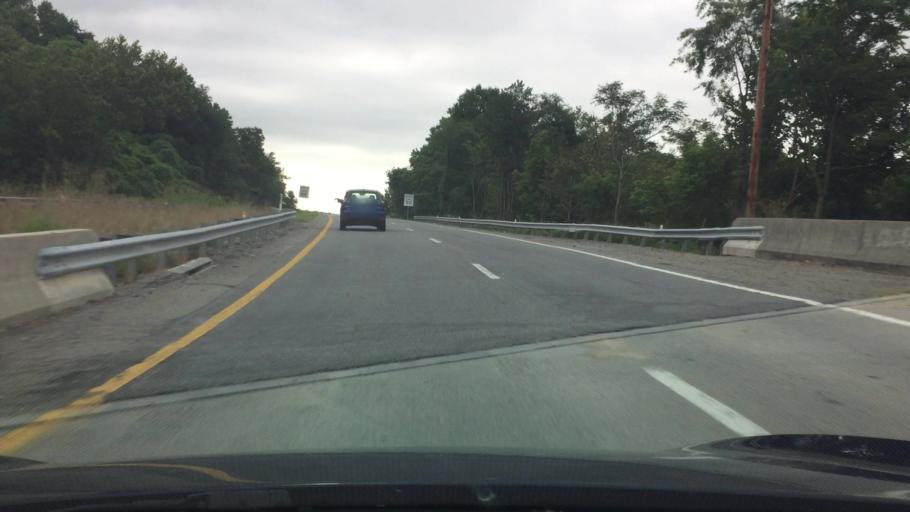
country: US
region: Virginia
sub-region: Montgomery County
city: Shawsville
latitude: 37.2221
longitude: -80.2191
